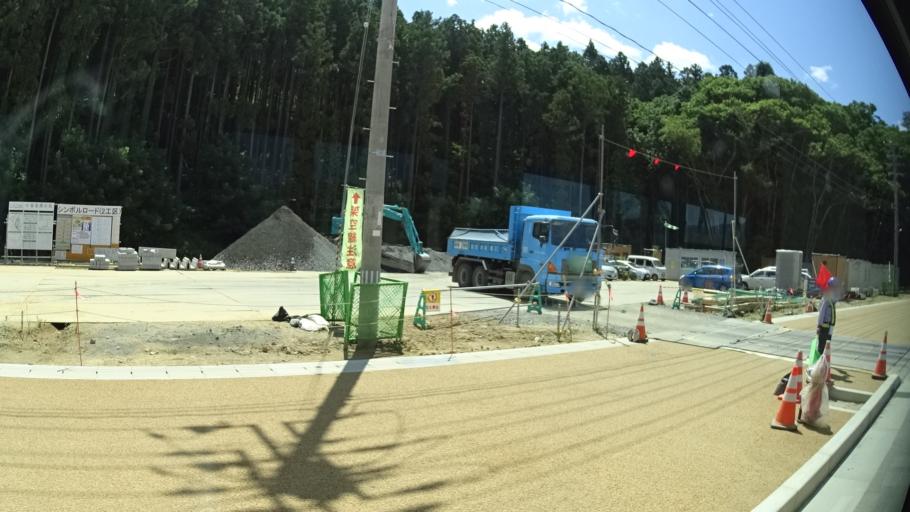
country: JP
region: Iwate
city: Ofunato
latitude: 39.0190
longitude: 141.6350
